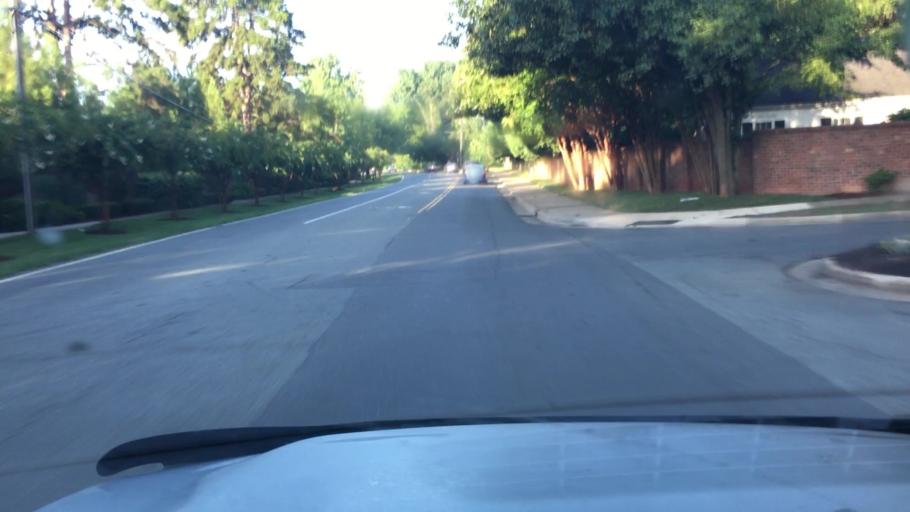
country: US
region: North Carolina
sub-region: Mecklenburg County
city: Matthews
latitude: 35.1292
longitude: -80.8135
